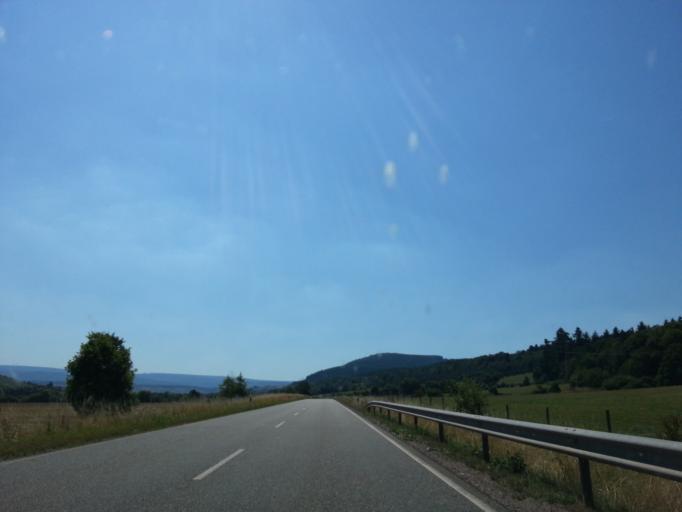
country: DE
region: Rheinland-Pfalz
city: Altrich
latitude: 49.9368
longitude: 6.9323
